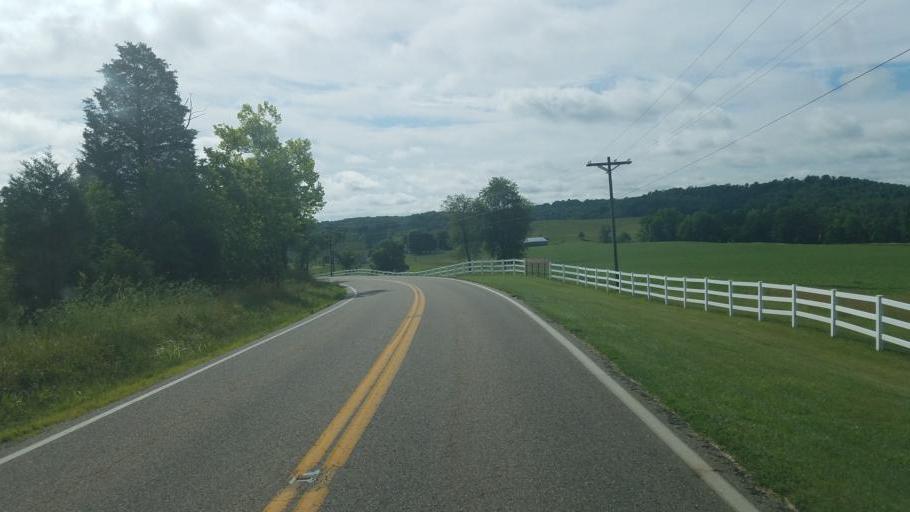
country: US
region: Ohio
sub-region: Gallia County
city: Gallipolis
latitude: 38.8311
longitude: -82.2721
